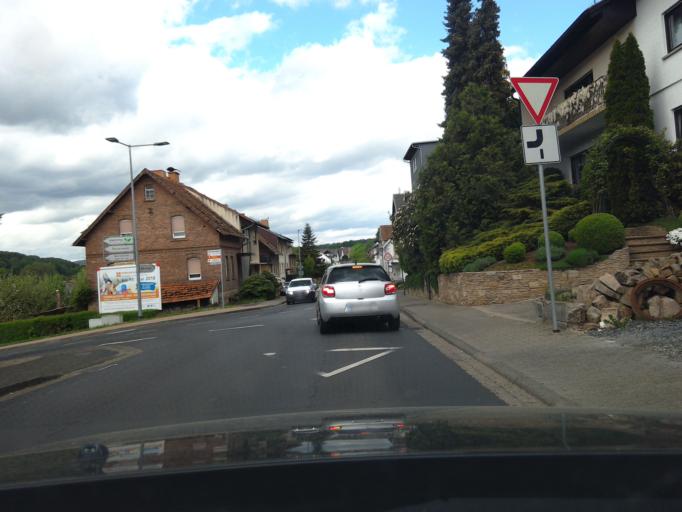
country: DE
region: Hesse
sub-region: Regierungsbezirk Darmstadt
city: Bad Orb
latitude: 50.2325
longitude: 9.3450
